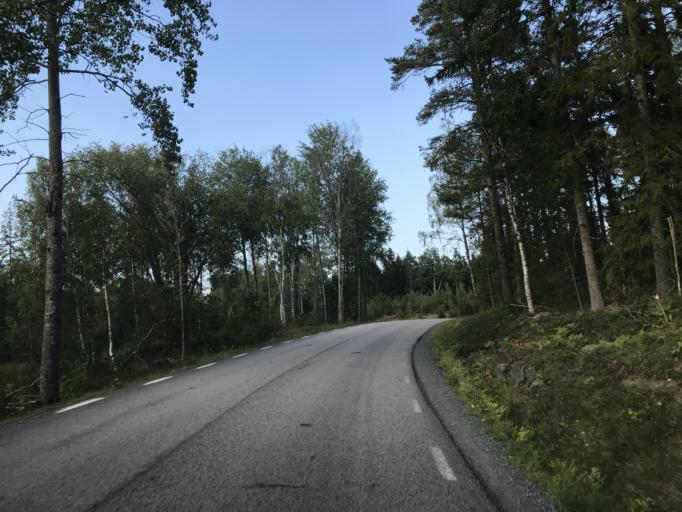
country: SE
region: Stockholm
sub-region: Norrtalje Kommun
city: Bjorko
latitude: 59.8717
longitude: 19.0128
